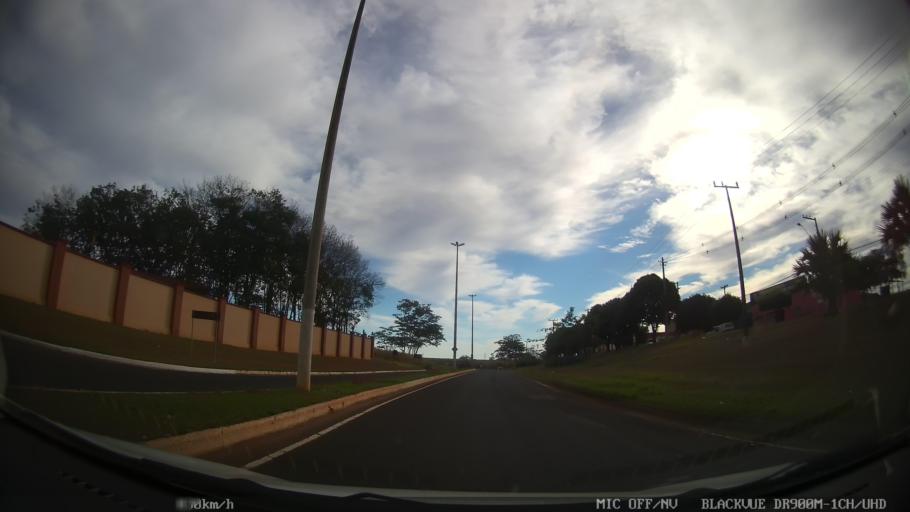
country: BR
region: Sao Paulo
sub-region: Catanduva
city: Catanduva
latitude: -21.1106
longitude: -48.9621
